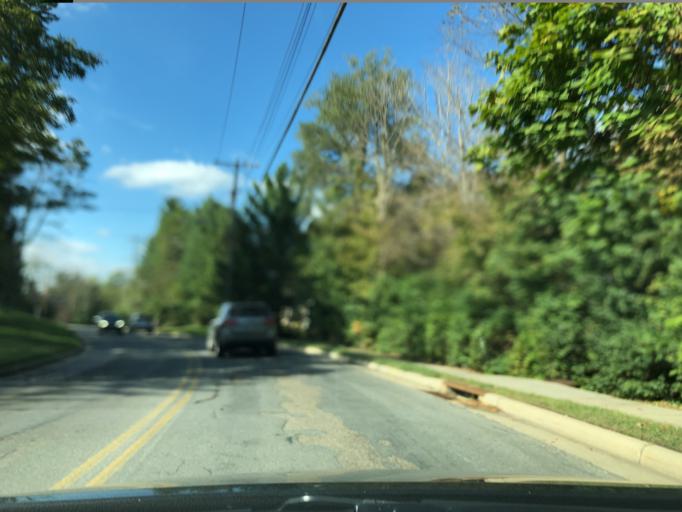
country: US
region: Ohio
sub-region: Hamilton County
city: Loveland
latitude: 39.2638
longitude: -84.2535
